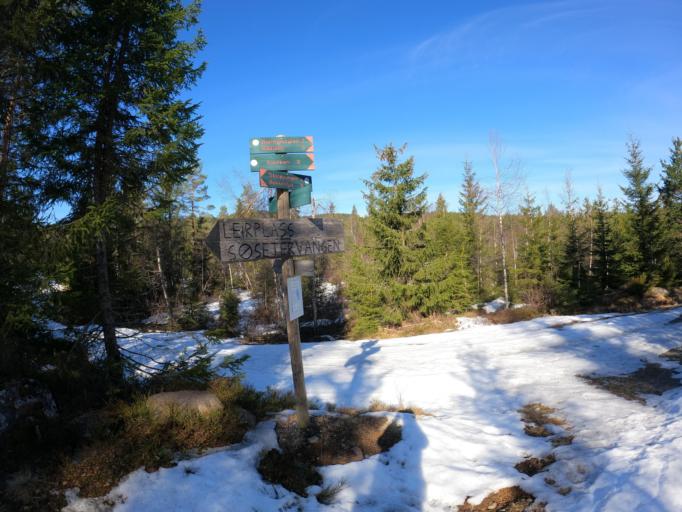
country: NO
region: Akershus
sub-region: Nittedal
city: Aneby
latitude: 60.1814
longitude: 10.8941
